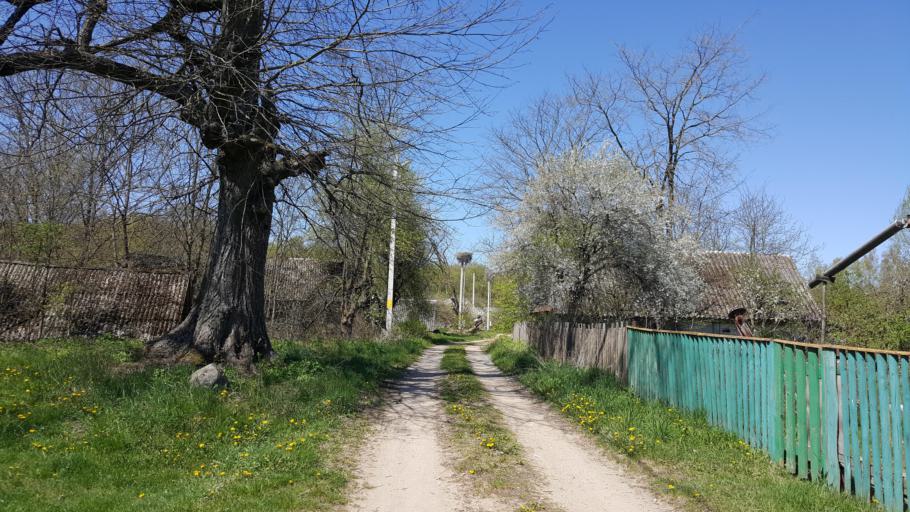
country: BY
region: Brest
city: Charnawchytsy
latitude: 52.3293
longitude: 23.6933
